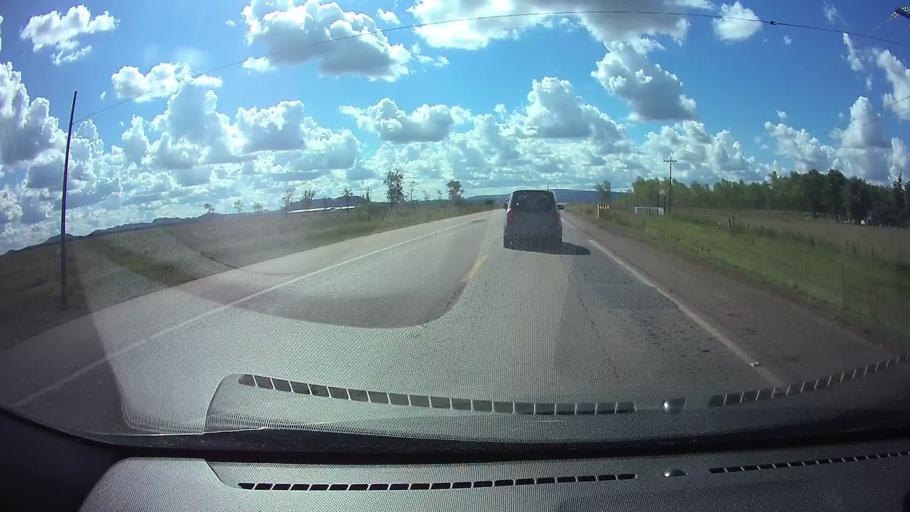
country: PY
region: Paraguari
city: Sapucai
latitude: -25.7444
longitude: -56.8064
